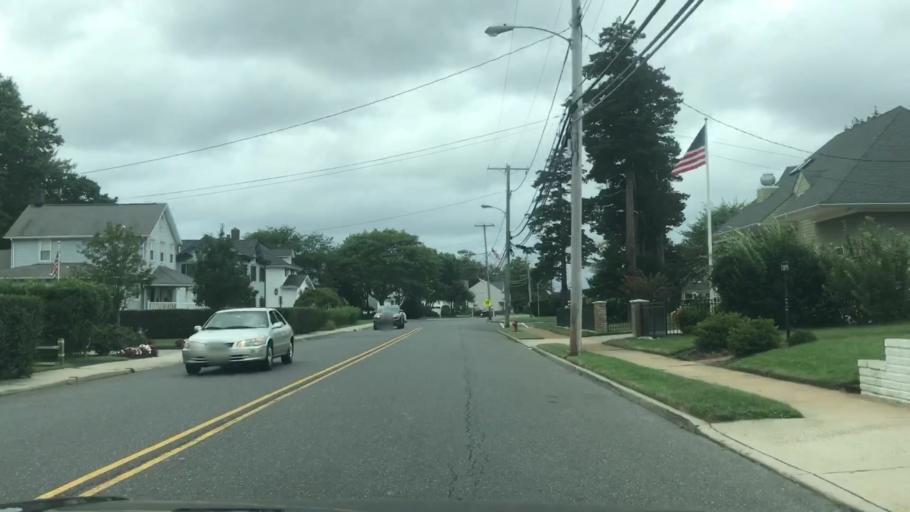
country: US
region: New Jersey
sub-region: Monmouth County
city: Monmouth Beach
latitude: 40.3316
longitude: -73.9831
